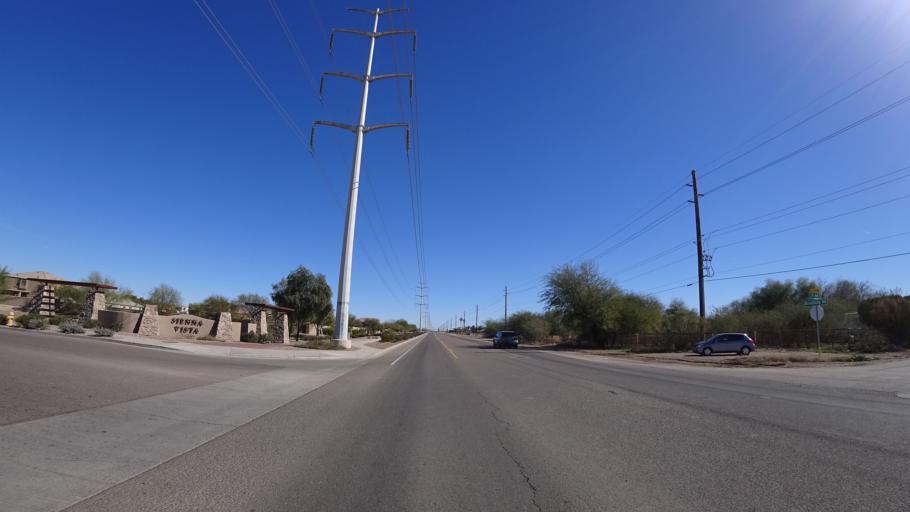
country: US
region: Arizona
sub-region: Maricopa County
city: Tolleson
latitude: 33.4085
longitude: -112.2131
